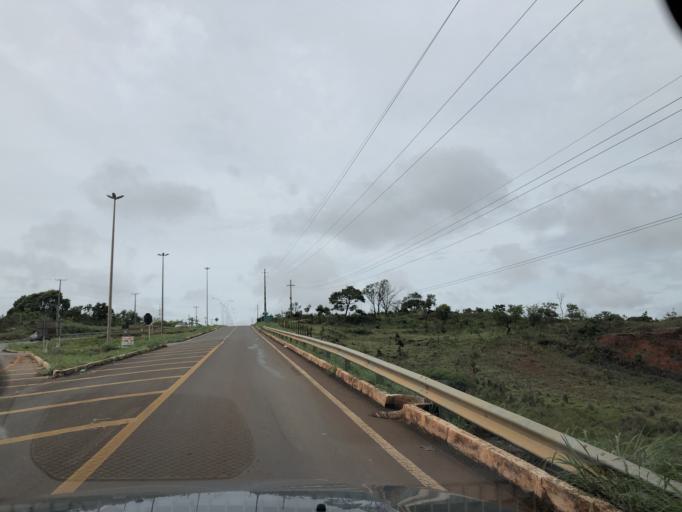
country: BR
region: Federal District
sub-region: Brasilia
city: Brasilia
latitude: -15.7745
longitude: -48.1291
